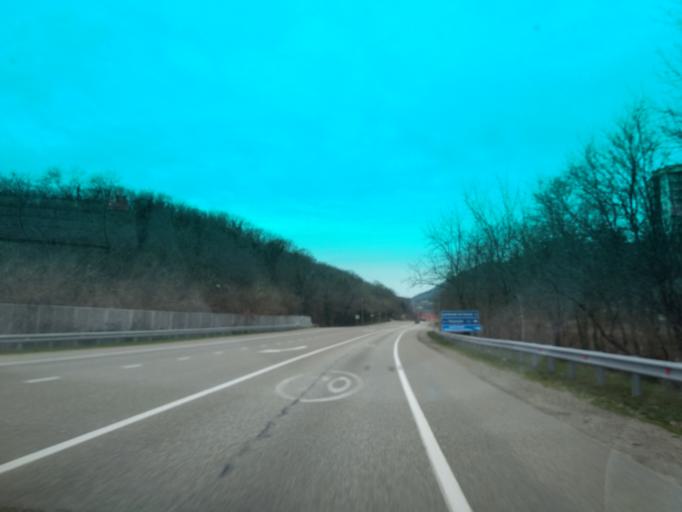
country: RU
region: Krasnodarskiy
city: Ol'ginka
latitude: 44.1876
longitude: 38.8922
